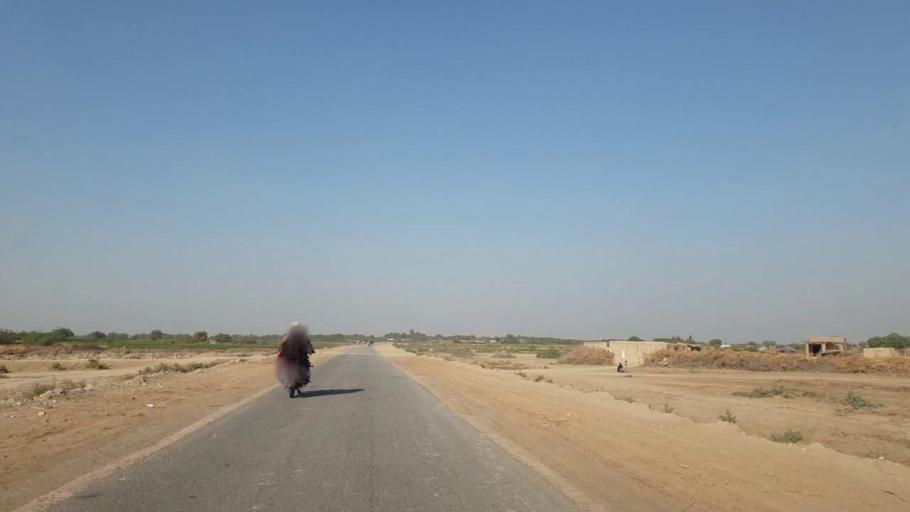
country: PK
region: Sindh
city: Digri
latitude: 25.1147
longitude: 69.1081
